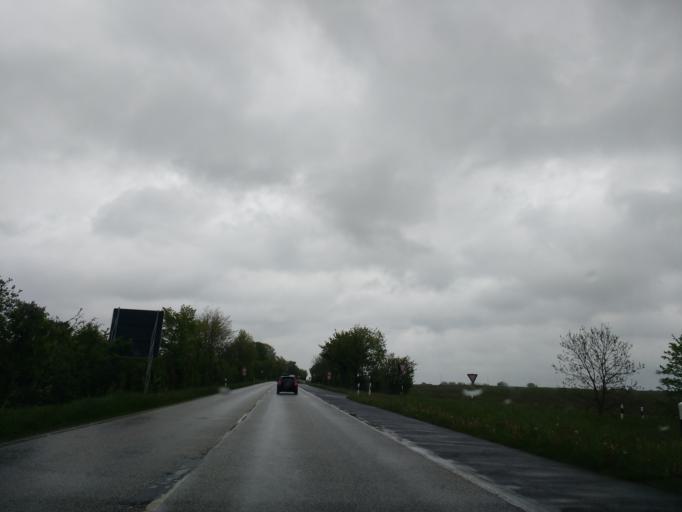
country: DE
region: Schleswig-Holstein
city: Barkelsby
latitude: 54.5010
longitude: 9.8493
